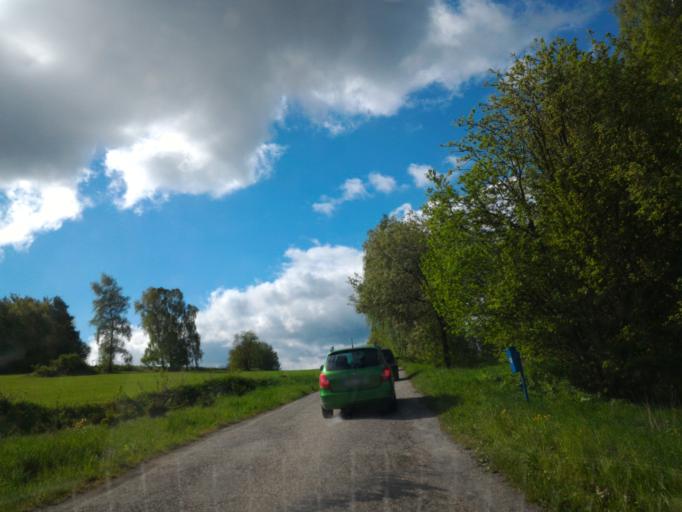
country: CZ
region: Vysocina
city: Ledec nad Sazavou
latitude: 49.6292
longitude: 15.3081
